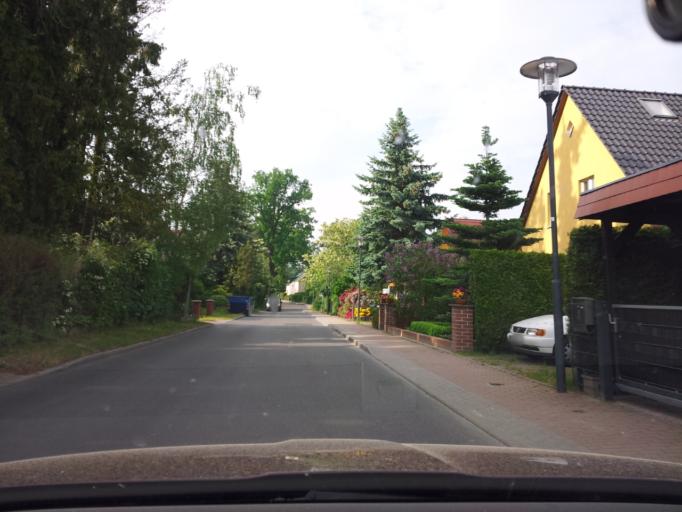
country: DE
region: Brandenburg
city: Werder
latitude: 52.3211
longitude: 12.9270
